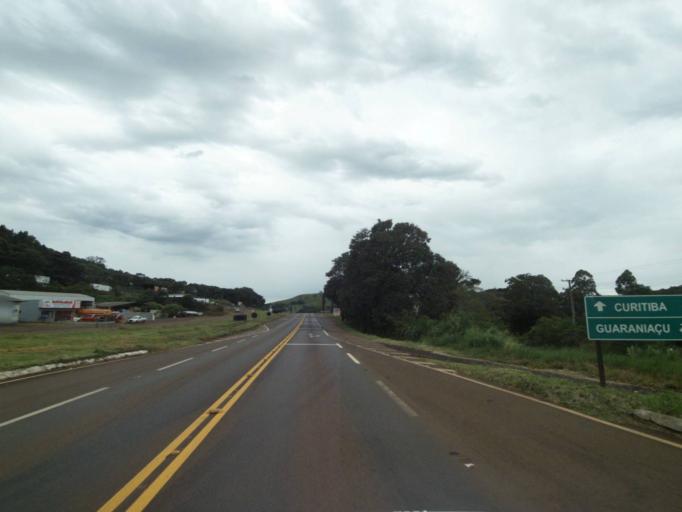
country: BR
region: Parana
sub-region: Guaraniacu
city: Guaraniacu
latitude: -25.1082
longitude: -52.8581
